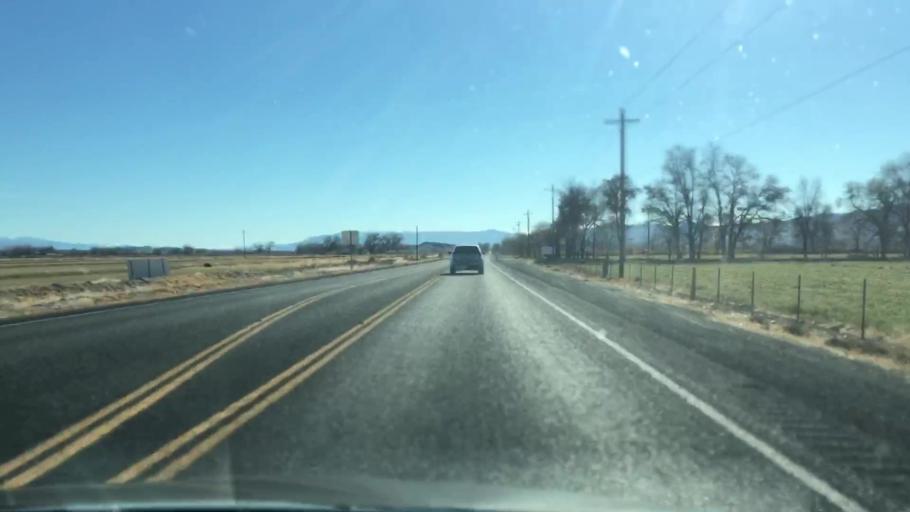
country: US
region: Nevada
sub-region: Lyon County
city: Yerington
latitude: 39.0691
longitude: -119.1812
